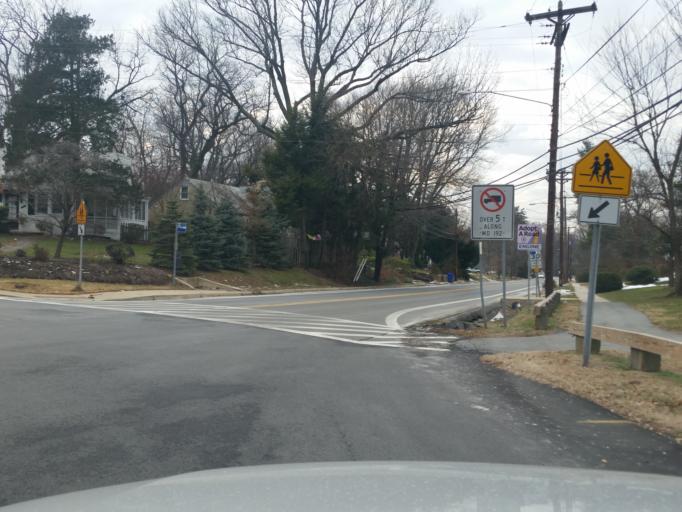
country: US
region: Maryland
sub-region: Montgomery County
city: Forest Glen
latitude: 39.0098
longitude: -77.0443
